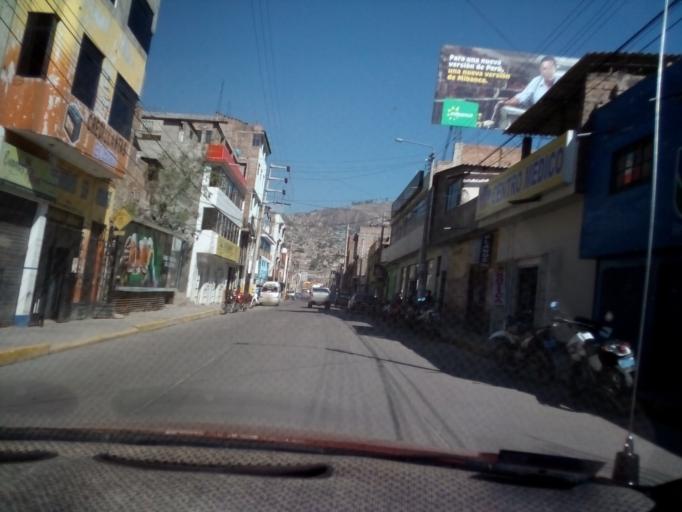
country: PE
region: Ayacucho
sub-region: Provincia de Huamanga
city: Ayacucho
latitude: -13.1643
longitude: -74.2185
